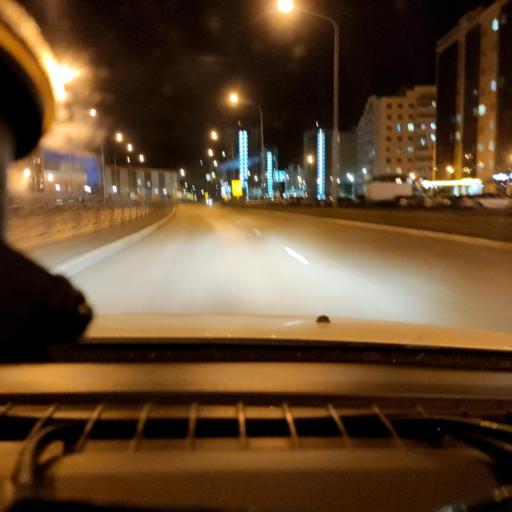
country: RU
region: Samara
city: Samara
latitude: 53.1103
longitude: 50.1409
